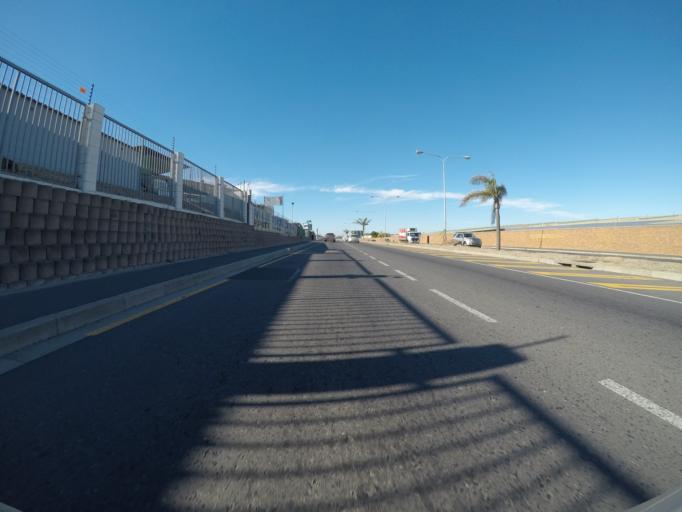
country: ZA
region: Western Cape
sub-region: City of Cape Town
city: Kraaifontein
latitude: -33.9056
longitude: 18.6675
